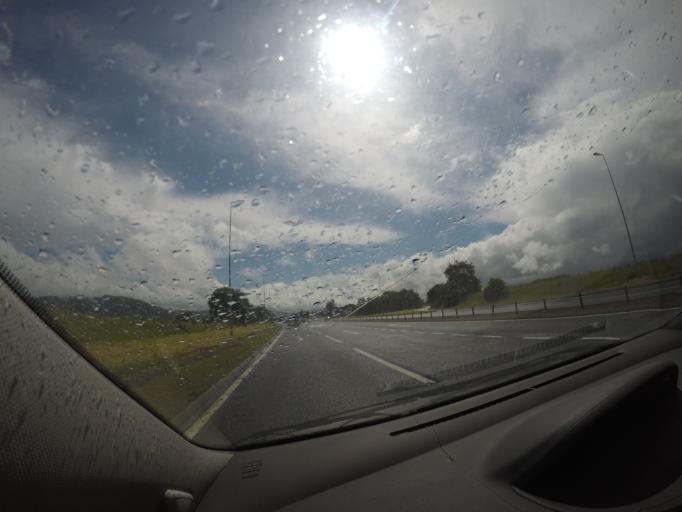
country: GB
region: Scotland
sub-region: Perth and Kinross
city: Auchterarder
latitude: 56.3239
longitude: -3.6454
